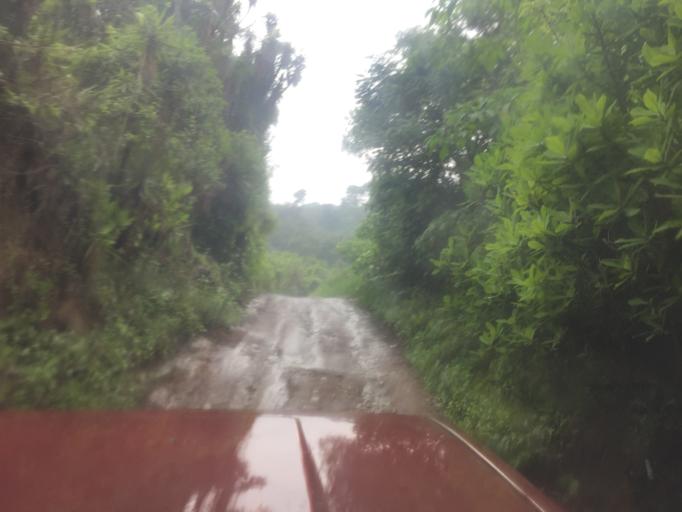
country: GT
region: Guatemala
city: Amatitlan
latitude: 14.5019
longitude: -90.6453
